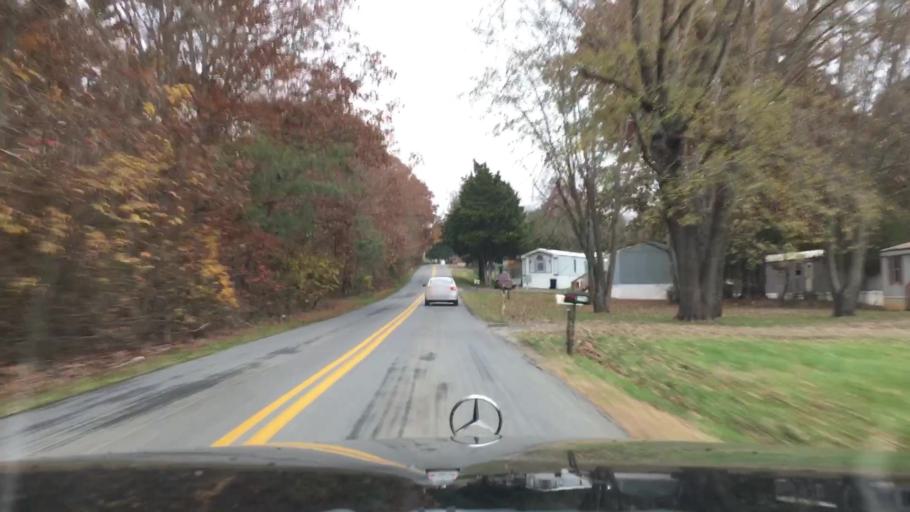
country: US
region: Virginia
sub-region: Campbell County
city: Timberlake
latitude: 37.2939
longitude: -79.2799
